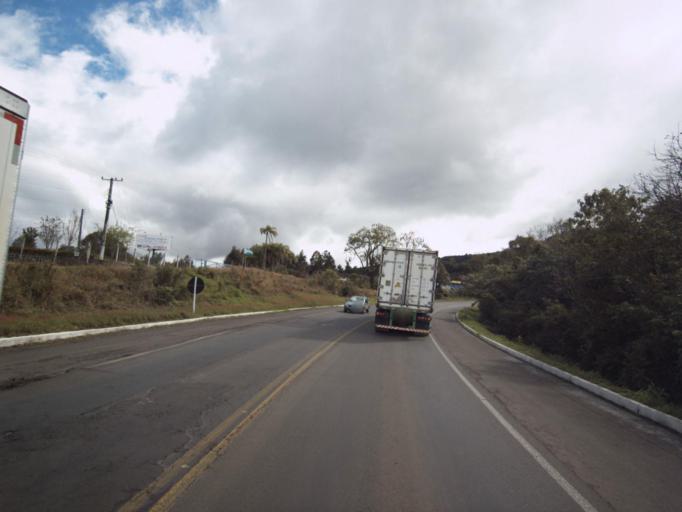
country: BR
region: Santa Catarina
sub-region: Concordia
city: Concordia
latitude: -27.2158
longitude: -51.9524
